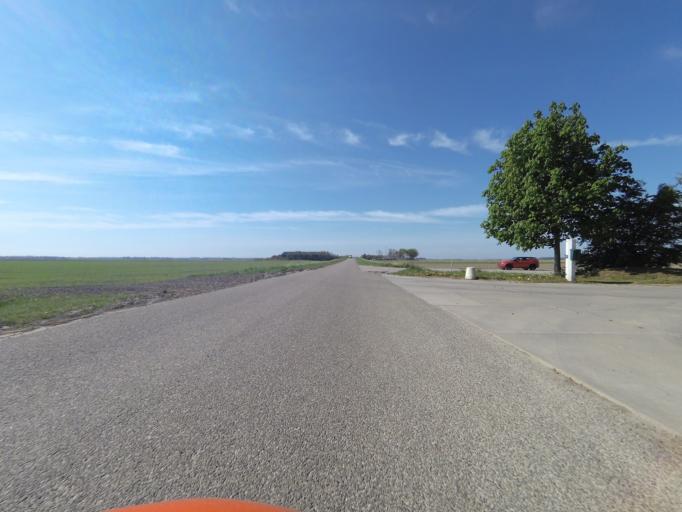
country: NL
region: Flevoland
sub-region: Gemeente Dronten
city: Dronten
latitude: 52.5727
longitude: 5.6959
